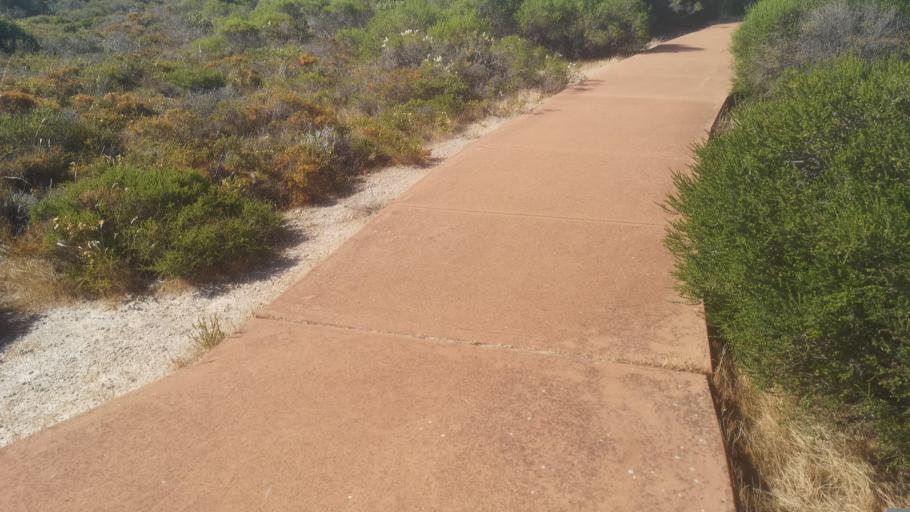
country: AU
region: Western Australia
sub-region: Dandaragan
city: Jurien Bay
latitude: -30.7921
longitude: 115.2250
